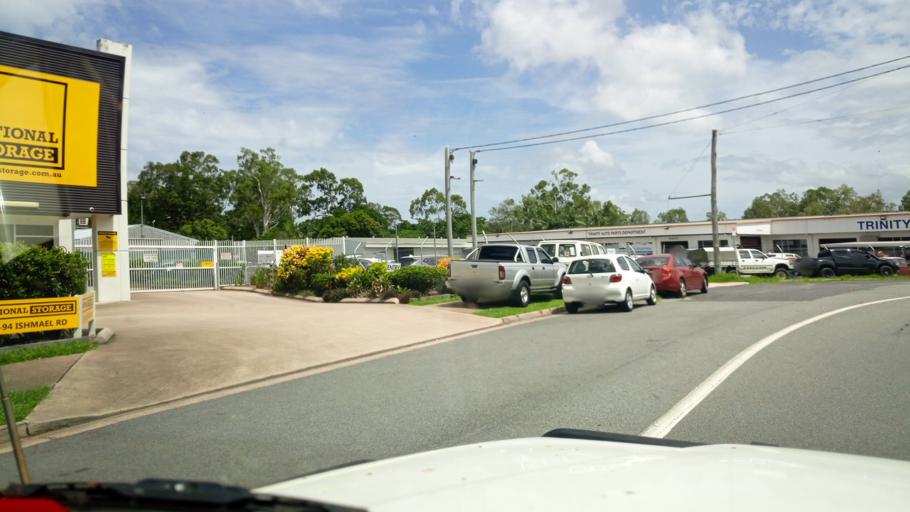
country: AU
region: Queensland
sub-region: Cairns
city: Woree
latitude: -16.9423
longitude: 145.7429
